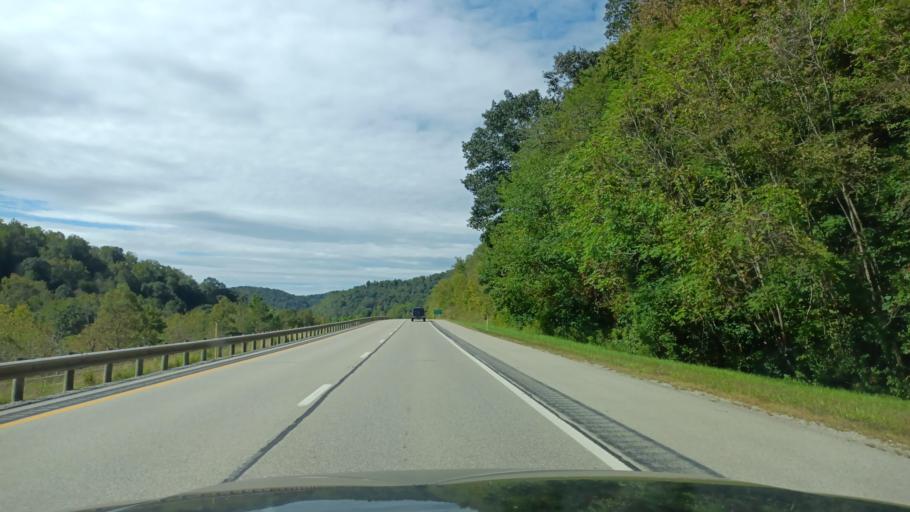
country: US
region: West Virginia
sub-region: Doddridge County
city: West Union
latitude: 39.2864
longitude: -80.7082
